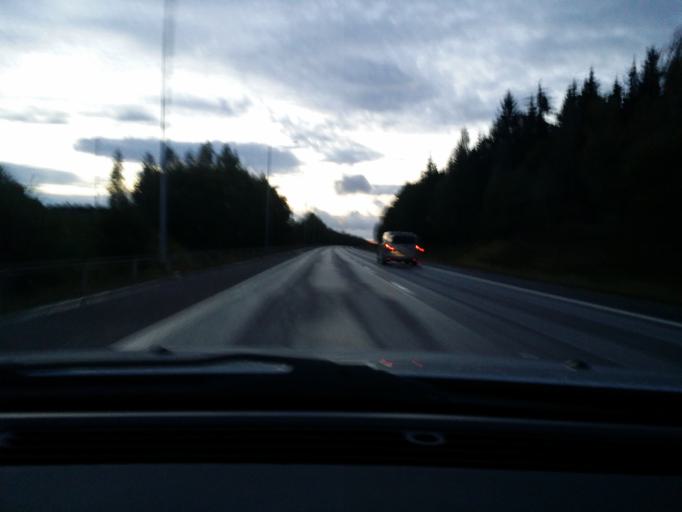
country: SE
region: Stockholm
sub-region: Upplands-Bro Kommun
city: Bro
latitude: 59.5145
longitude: 17.6784
